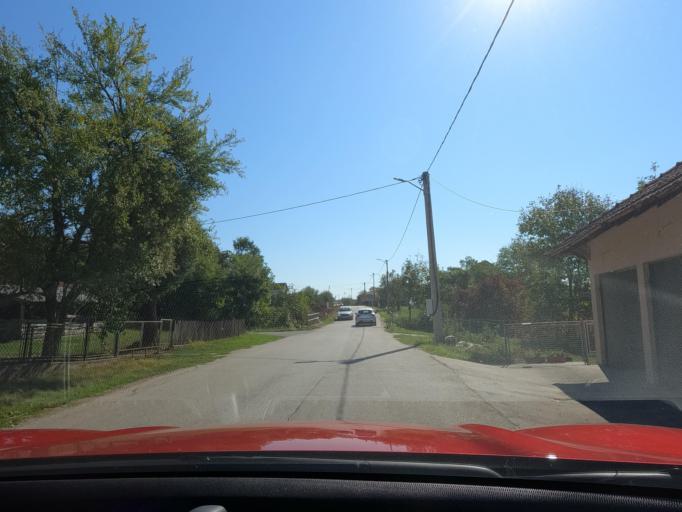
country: RS
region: Central Serbia
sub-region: Raski Okrug
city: Kraljevo
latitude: 43.7603
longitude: 20.6797
